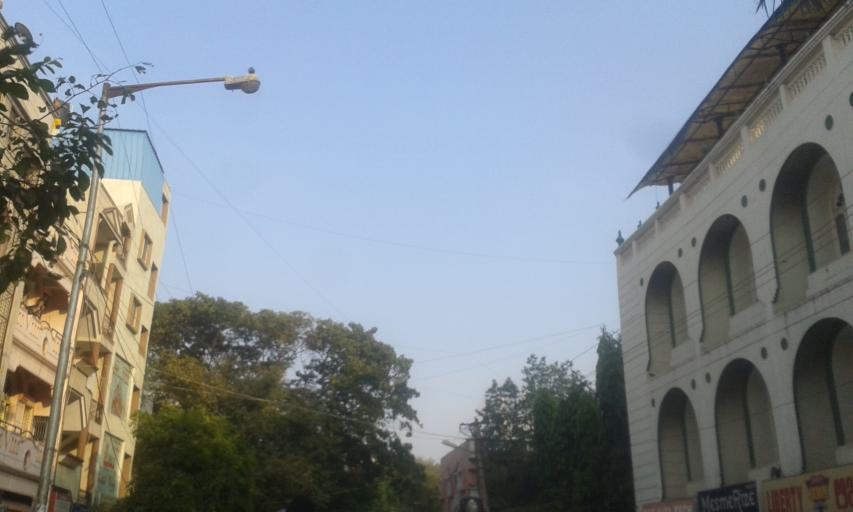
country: IN
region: Karnataka
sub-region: Bangalore Urban
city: Bangalore
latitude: 12.9206
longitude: 77.5939
